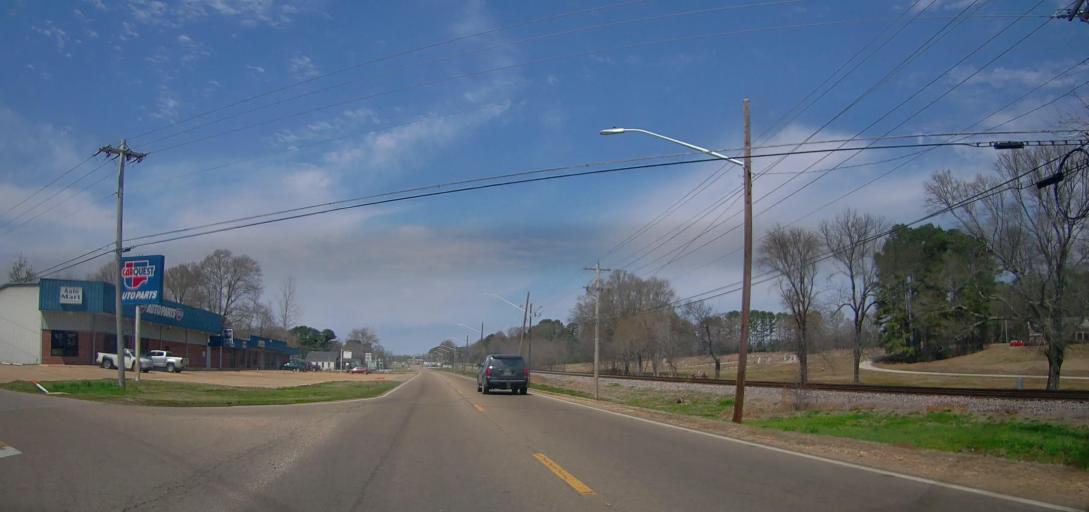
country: US
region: Mississippi
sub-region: Union County
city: New Albany
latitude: 34.5040
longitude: -89.0286
